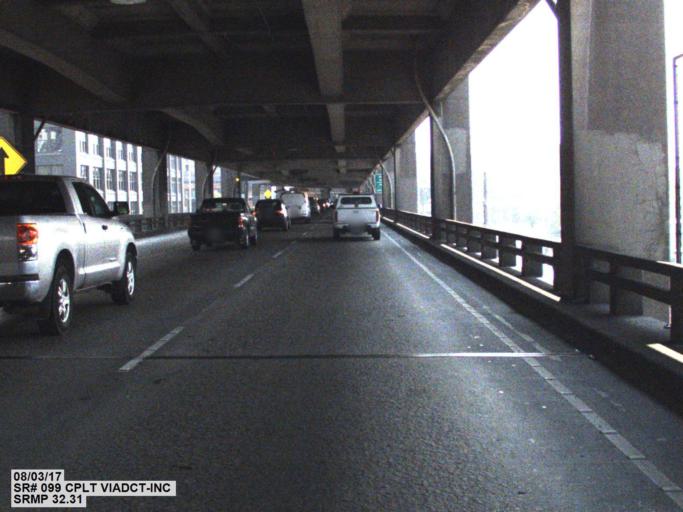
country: US
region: Washington
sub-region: Pierce County
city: Fife
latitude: 47.2430
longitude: -122.3482
